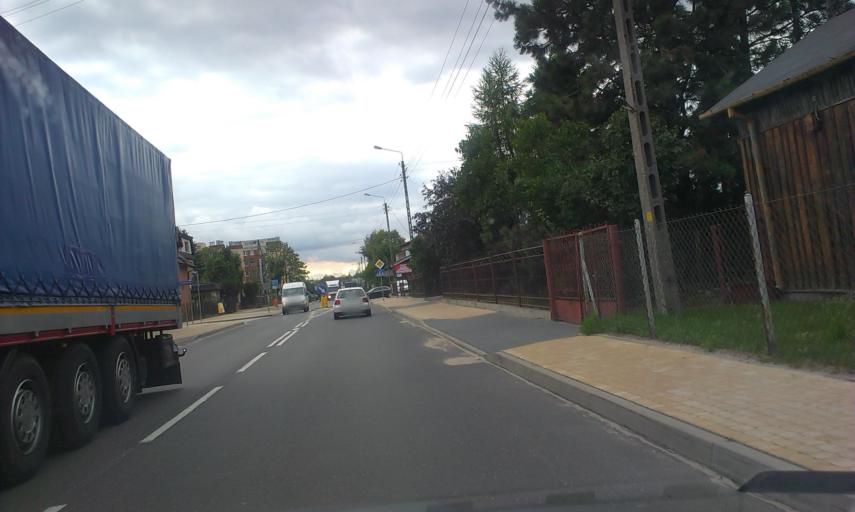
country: PL
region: Masovian Voivodeship
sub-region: Powiat zyrardowski
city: Mszczonow
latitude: 51.9740
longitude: 20.5257
